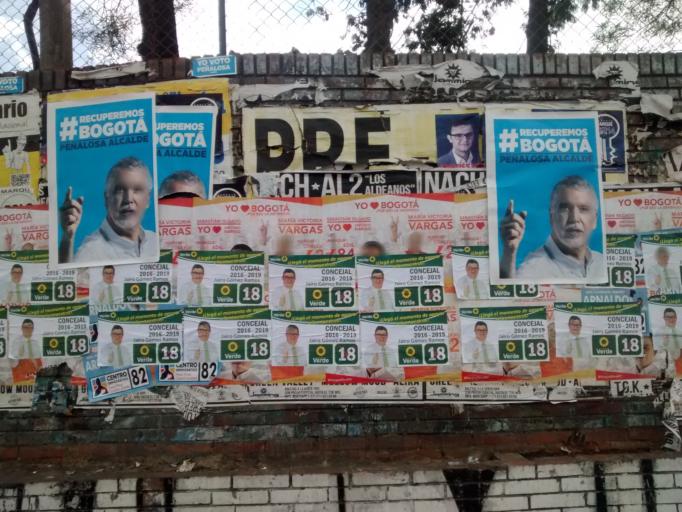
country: CO
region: Bogota D.C.
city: Bogota
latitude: 4.5856
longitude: -74.0943
